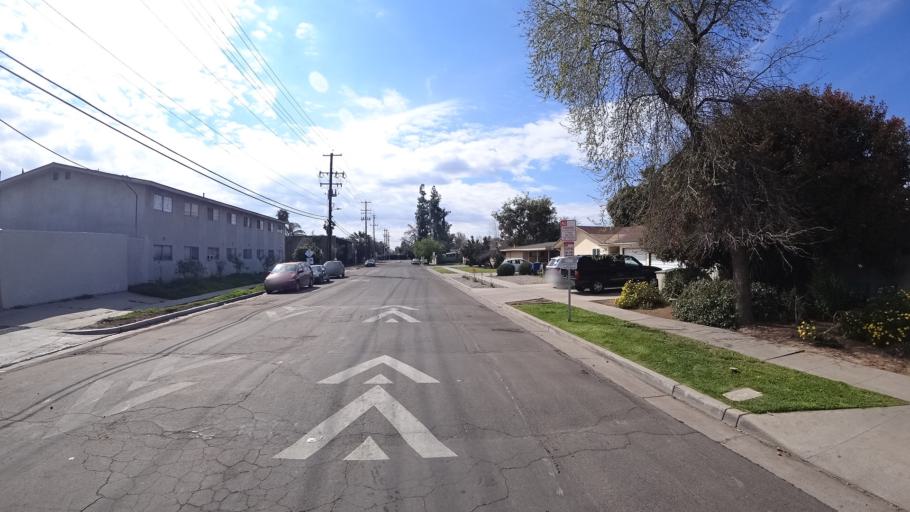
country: US
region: California
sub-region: Fresno County
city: Clovis
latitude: 36.8136
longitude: -119.7655
